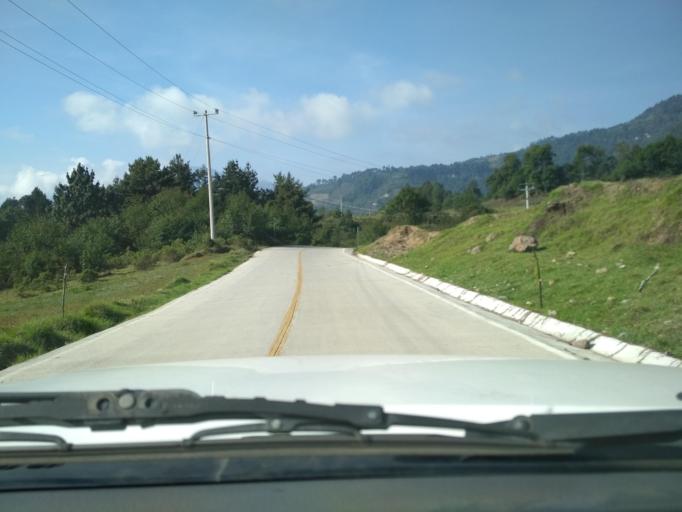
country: MX
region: Veracruz
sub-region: La Perla
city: Chilapa
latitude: 19.0025
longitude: -97.1821
